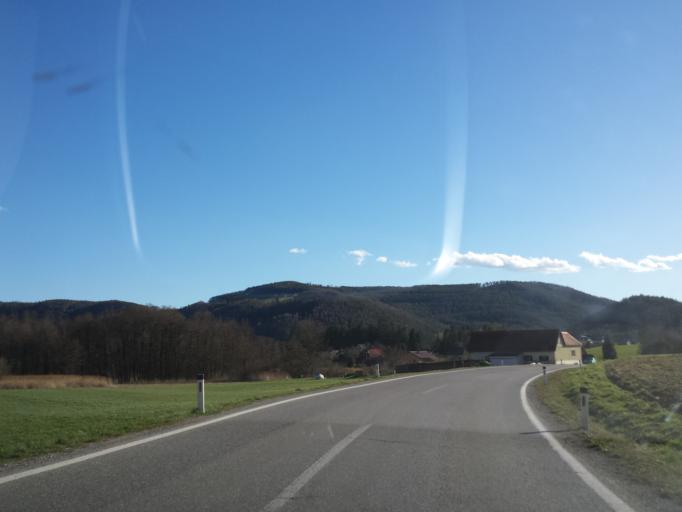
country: AT
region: Styria
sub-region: Politischer Bezirk Graz-Umgebung
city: Sankt Radegund bei Graz
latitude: 47.1472
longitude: 15.4809
